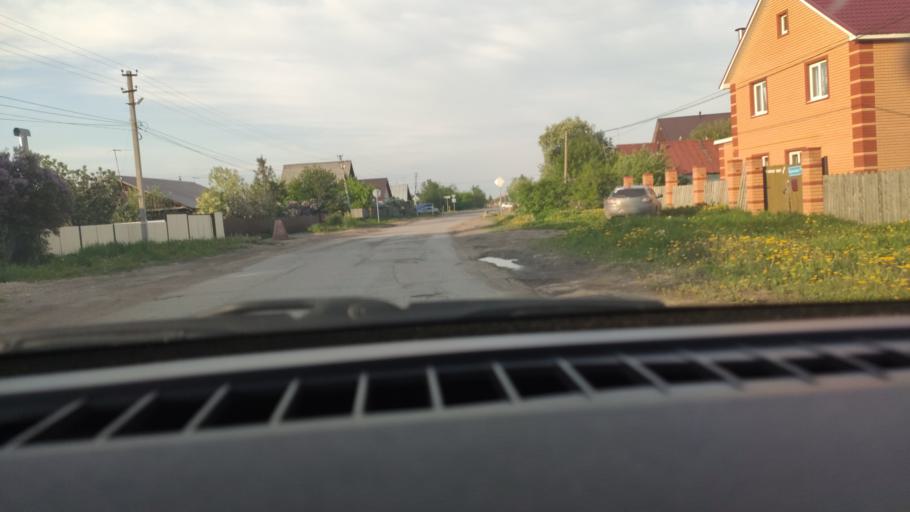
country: RU
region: Perm
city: Kultayevo
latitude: 57.9346
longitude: 56.0223
